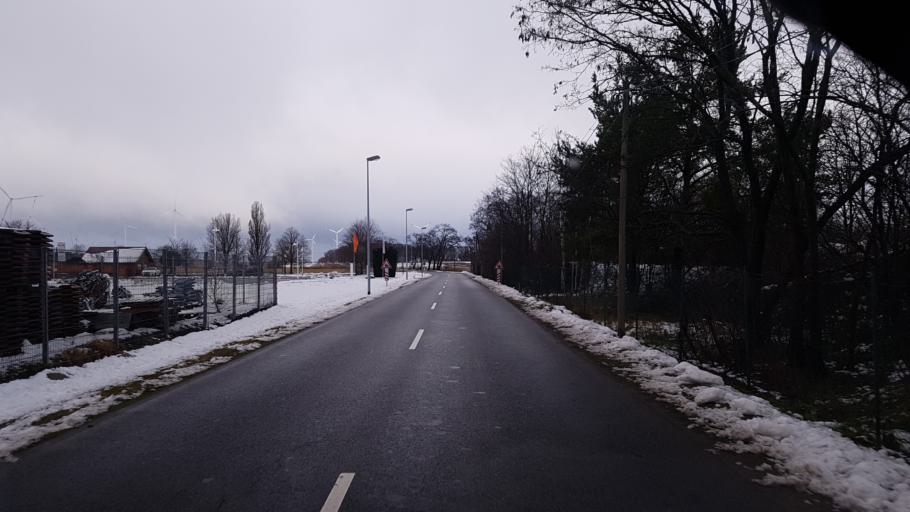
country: DE
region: Brandenburg
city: Luckau
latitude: 51.8790
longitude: 13.7955
